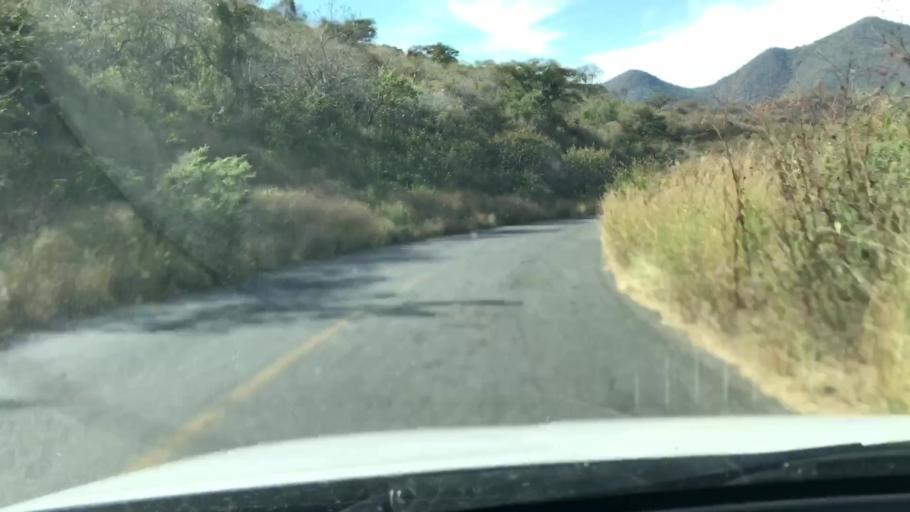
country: MX
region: Jalisco
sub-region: Zacoalco de Torres
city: Barranca de Otates (Barranca de Otatan)
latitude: 20.2499
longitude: -103.6692
